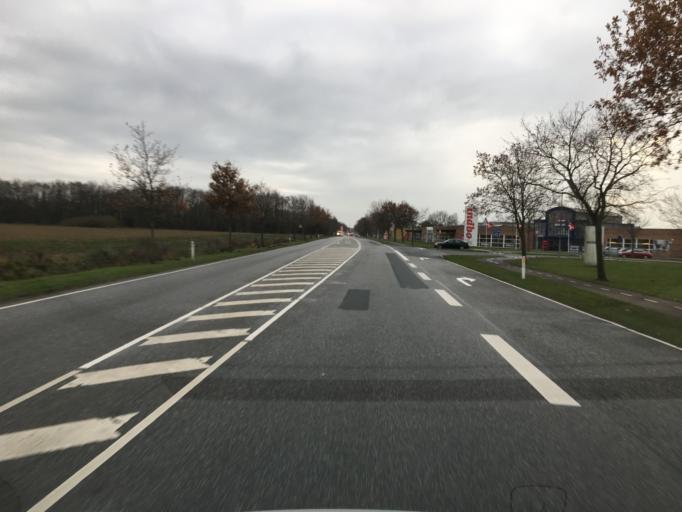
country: DK
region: South Denmark
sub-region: Tonder Kommune
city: Tonder
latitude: 54.9556
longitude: 8.8696
